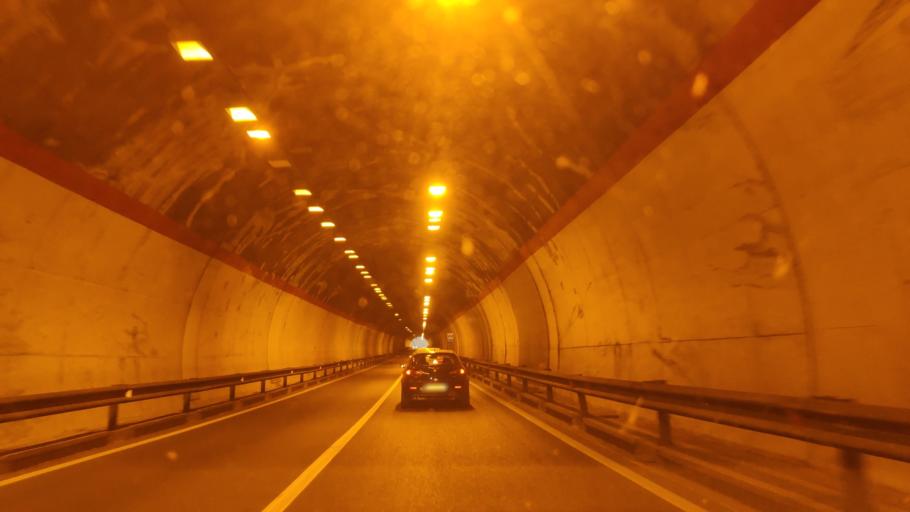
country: IT
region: Calabria
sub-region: Provincia di Cosenza
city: Marina
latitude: 39.4712
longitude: 15.9795
